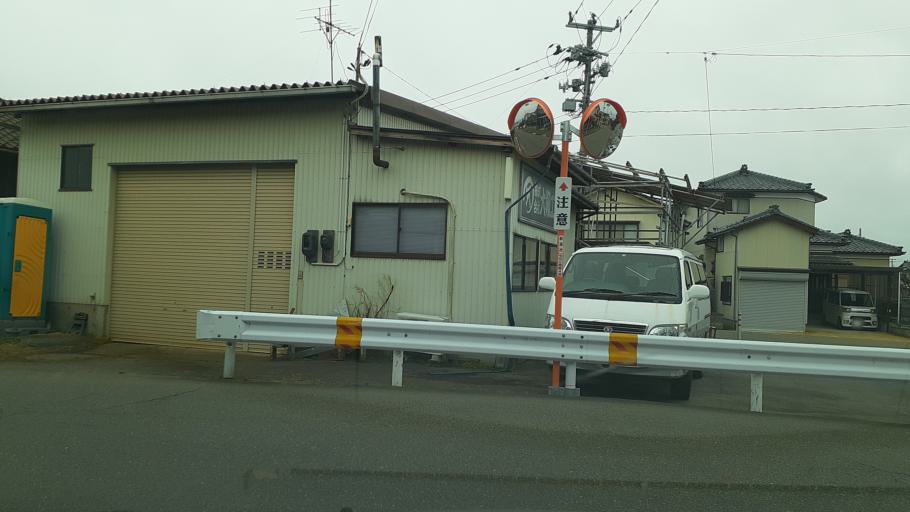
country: JP
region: Niigata
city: Niigata-shi
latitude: 37.8598
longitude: 139.0378
